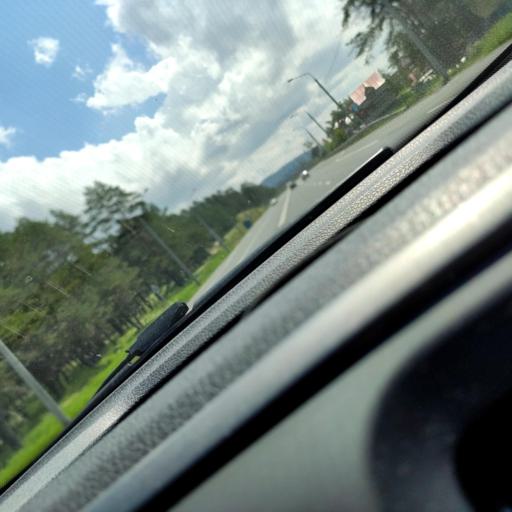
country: RU
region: Samara
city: Volzhskiy
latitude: 53.4396
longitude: 50.1084
